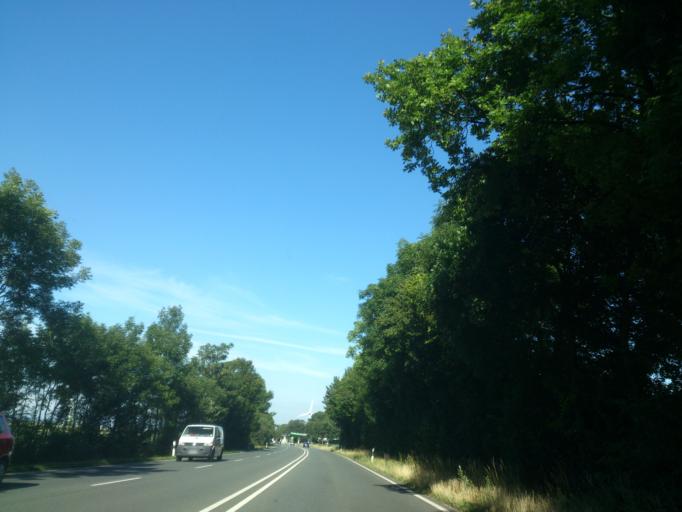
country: DE
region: North Rhine-Westphalia
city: Bad Lippspringe
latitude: 51.7221
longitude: 8.8574
